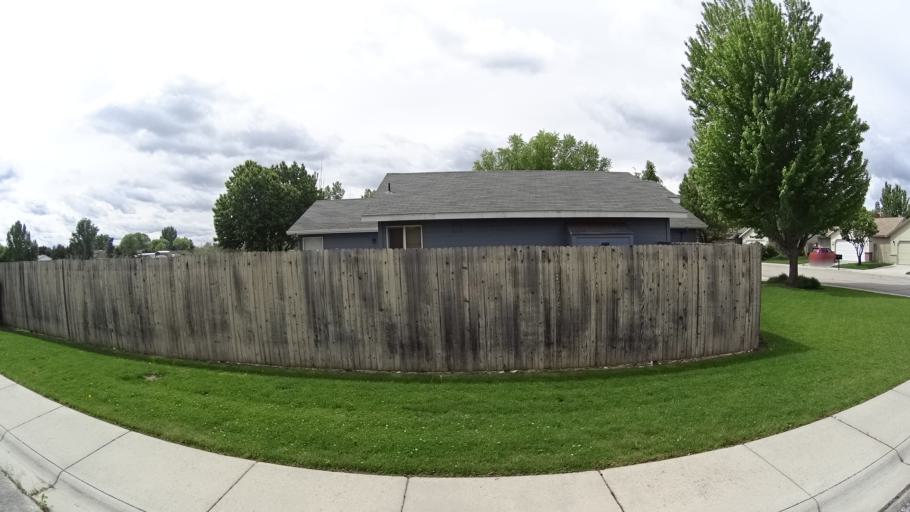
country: US
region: Idaho
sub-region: Ada County
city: Eagle
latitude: 43.6807
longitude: -116.2993
